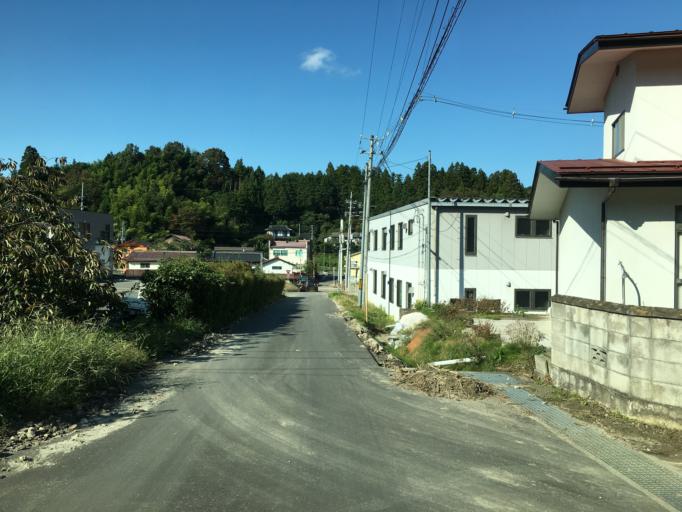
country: JP
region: Fukushima
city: Fukushima-shi
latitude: 37.6645
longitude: 140.5801
